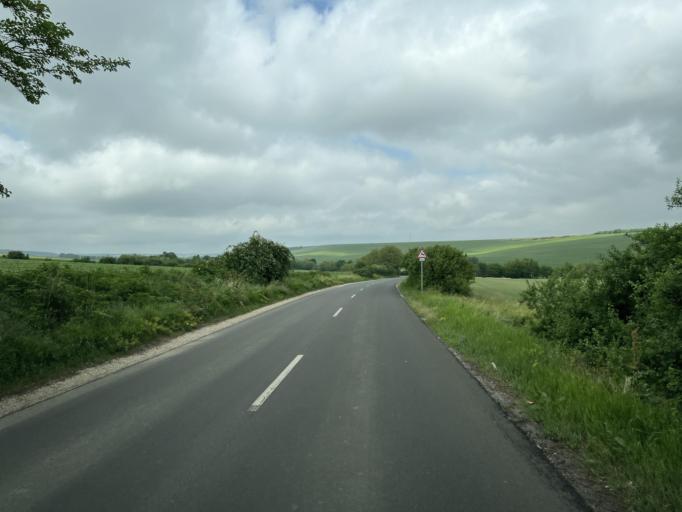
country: HU
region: Pest
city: Kartal
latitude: 47.7305
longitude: 19.5297
